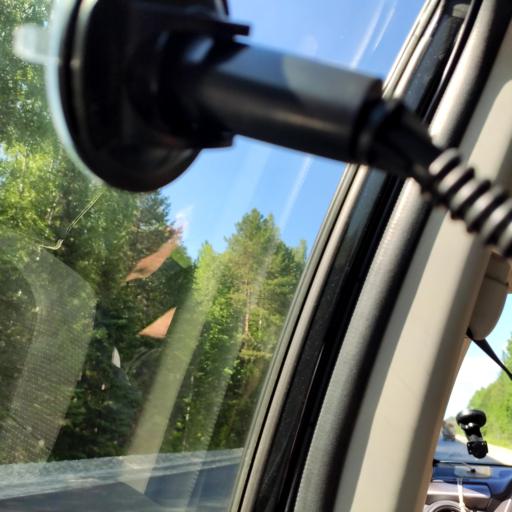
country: RU
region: Mariy-El
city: Suslonger
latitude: 56.2639
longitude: 48.2328
